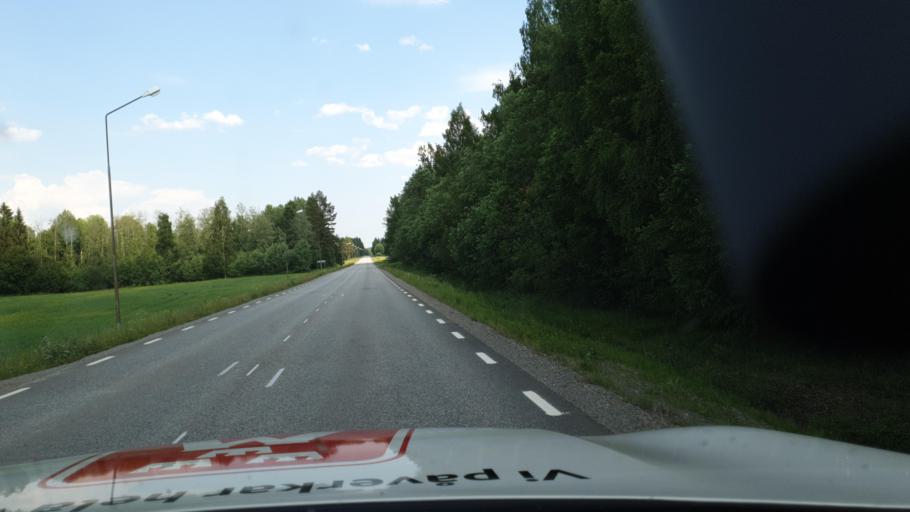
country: SE
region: Vaesterbotten
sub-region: Skelleftea Kommun
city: Viken
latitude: 64.7399
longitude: 20.7911
